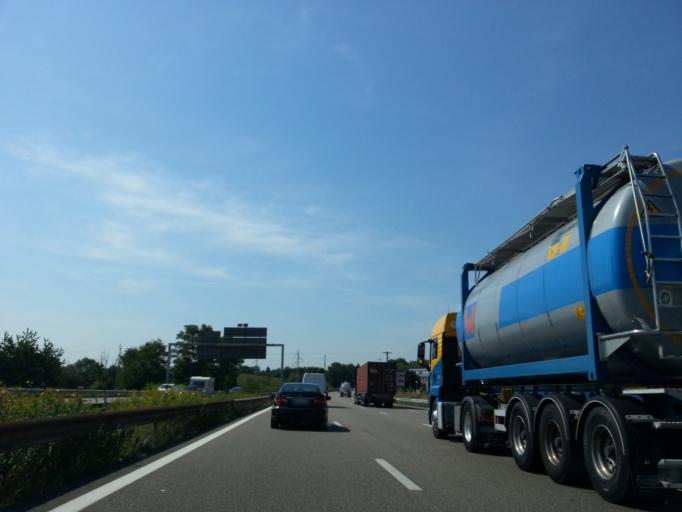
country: FR
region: Alsace
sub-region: Departement du Bas-Rhin
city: Souffelweyersheim
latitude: 48.6431
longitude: 7.7318
